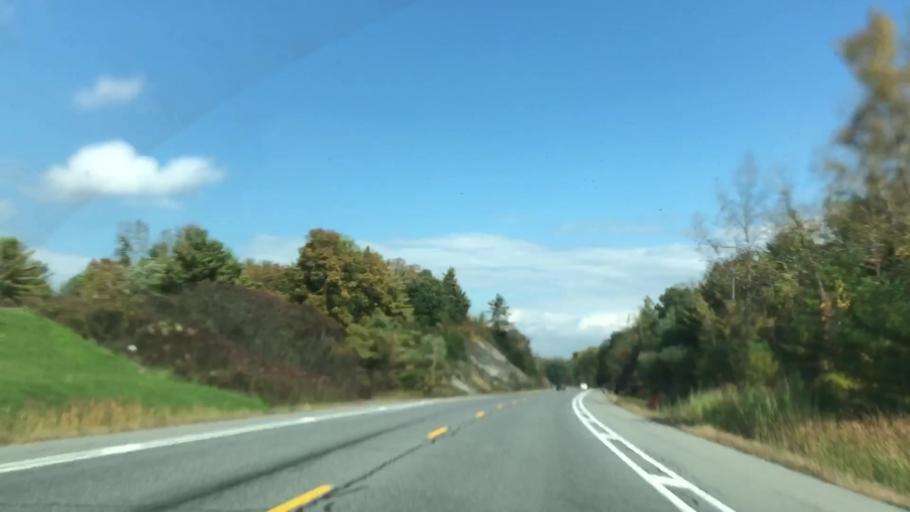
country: US
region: New York
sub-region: Washington County
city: Whitehall
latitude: 43.4692
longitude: -73.4372
